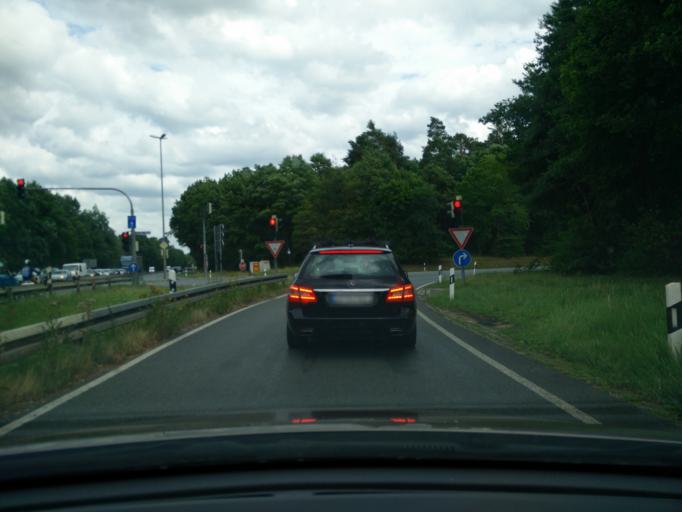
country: DE
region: Bavaria
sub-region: Regierungsbezirk Mittelfranken
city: Schwaig
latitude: 49.4210
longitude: 11.1591
